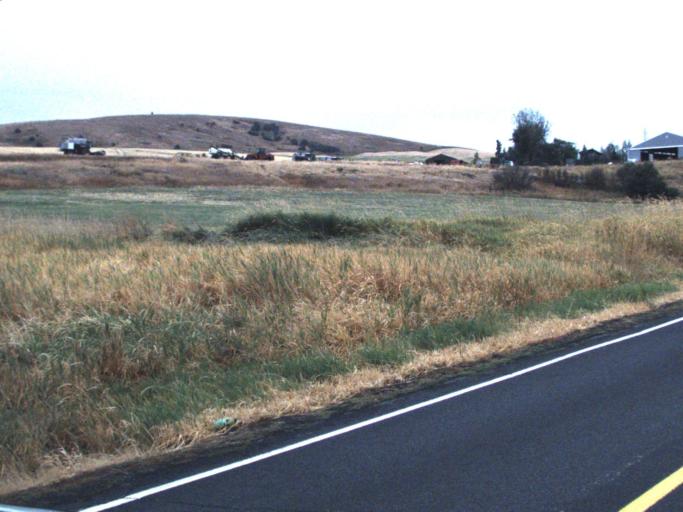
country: US
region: Washington
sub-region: Spokane County
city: Medical Lake
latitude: 47.7203
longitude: -117.8712
